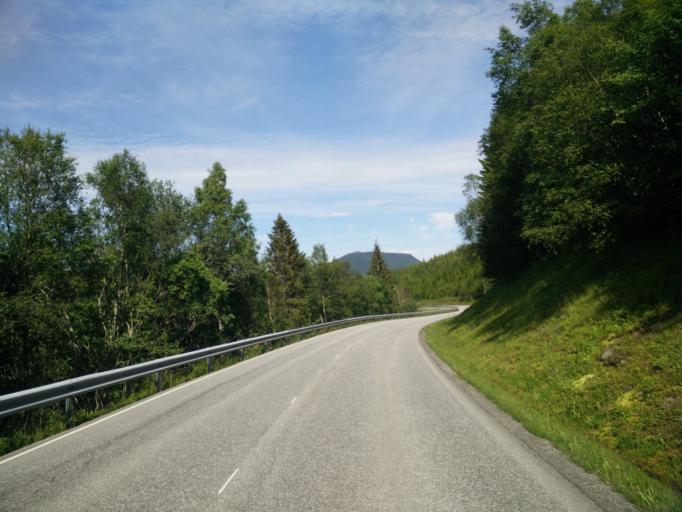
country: NO
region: More og Romsdal
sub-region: Kristiansund
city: Rensvik
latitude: 63.0256
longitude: 8.0197
